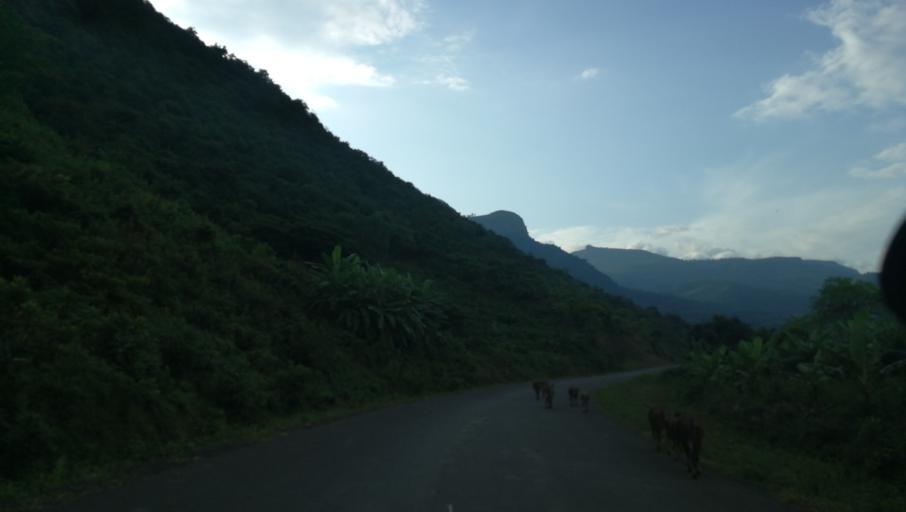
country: ET
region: Southern Nations, Nationalities, and People's Region
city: Areka
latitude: 6.8550
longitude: 37.2654
